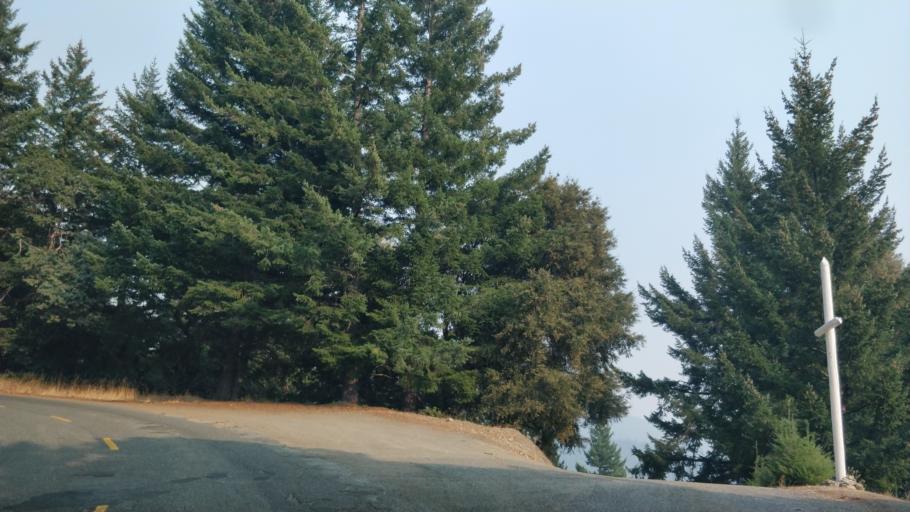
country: US
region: California
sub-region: Humboldt County
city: Rio Dell
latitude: 40.2676
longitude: -124.0776
